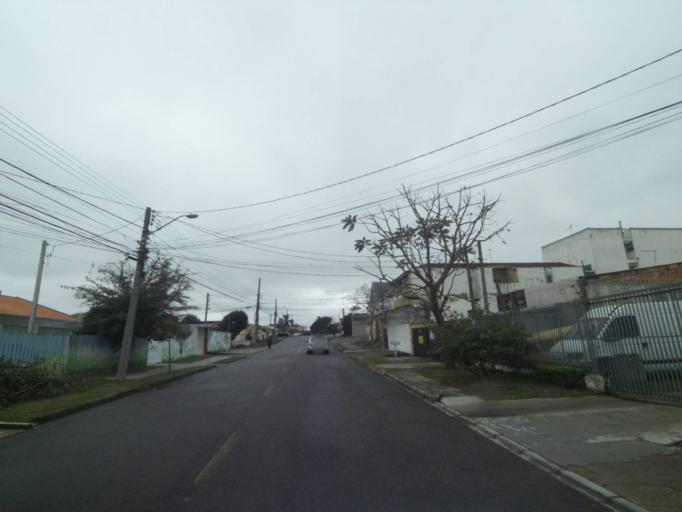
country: BR
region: Parana
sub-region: Curitiba
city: Curitiba
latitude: -25.5068
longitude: -49.3015
